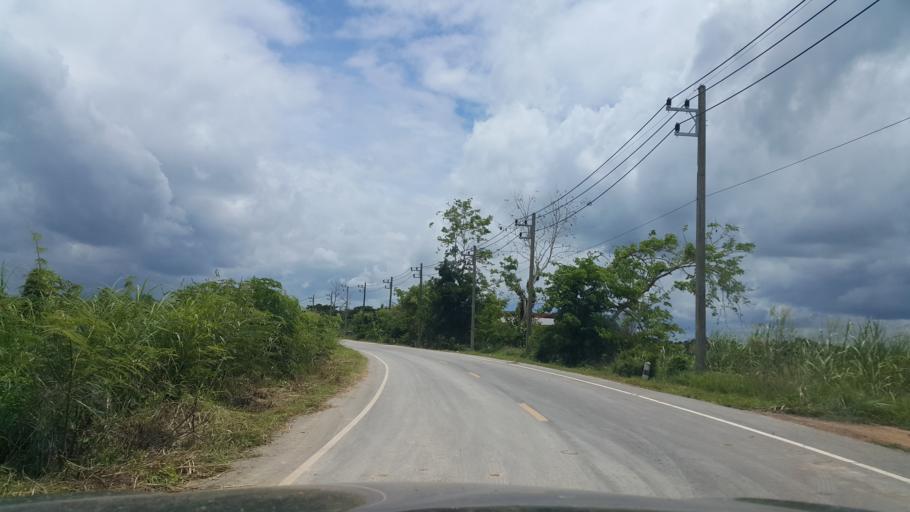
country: TH
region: Sukhothai
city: Kong Krailat
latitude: 16.9340
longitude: 99.9487
